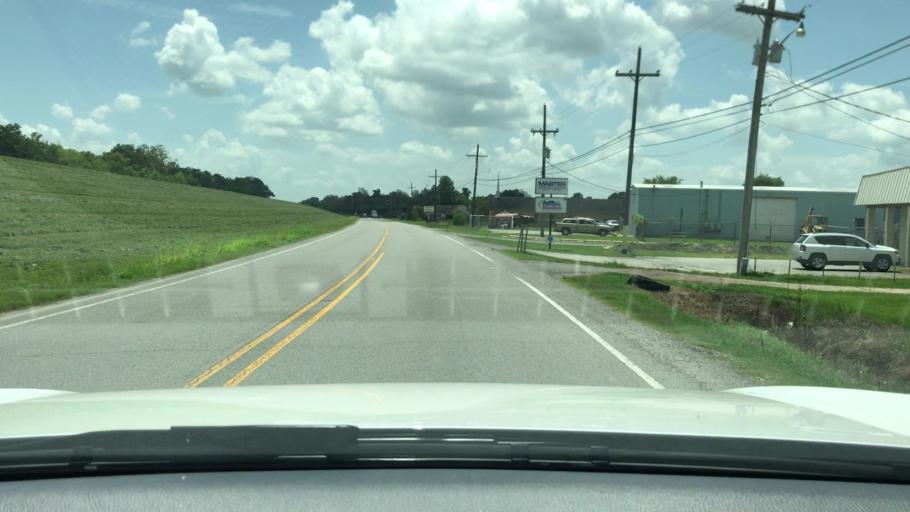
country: US
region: Louisiana
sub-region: Iberville Parish
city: Plaquemine
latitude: 30.2811
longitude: -91.2224
